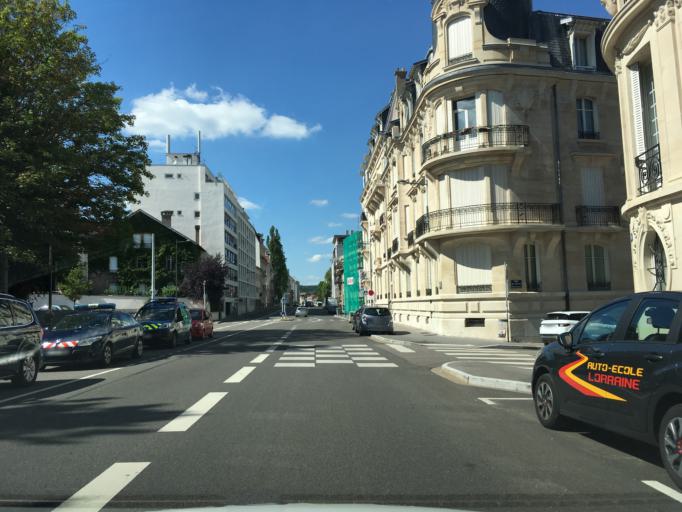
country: FR
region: Lorraine
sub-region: Departement de Meurthe-et-Moselle
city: Maxeville
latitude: 48.6937
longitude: 6.1679
